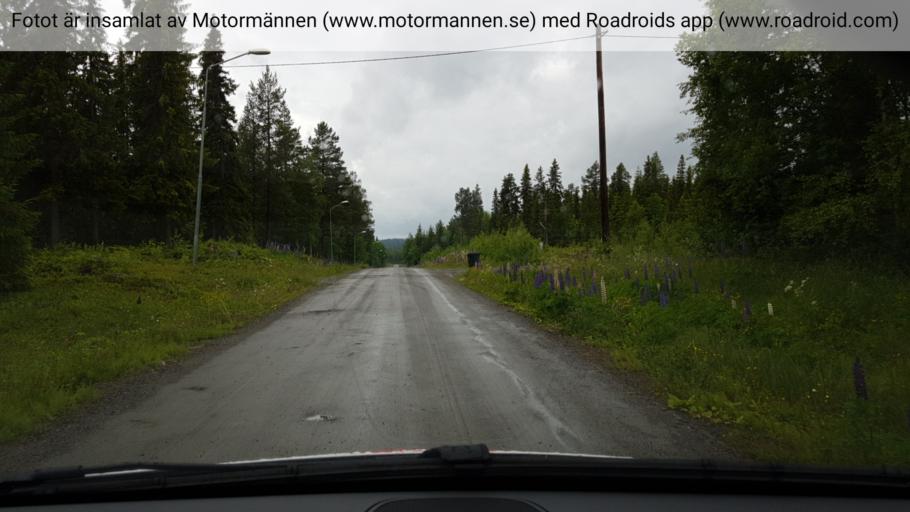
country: SE
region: Jaemtland
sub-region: Stroemsunds Kommun
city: Stroemsund
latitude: 64.2826
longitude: 15.0148
